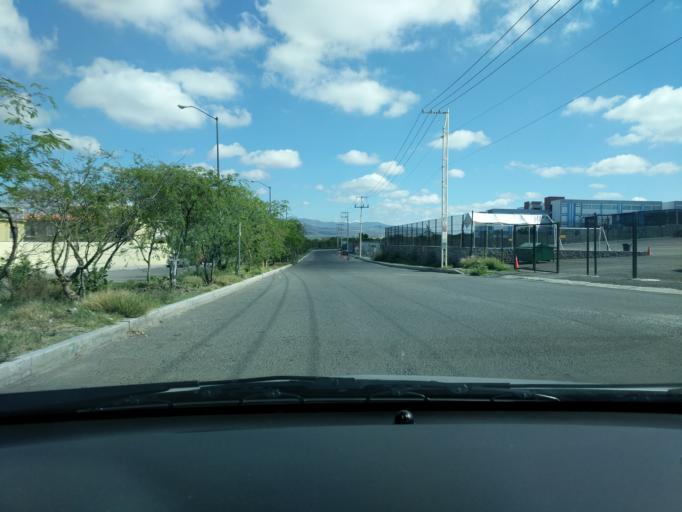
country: MX
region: Queretaro
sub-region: Queretaro
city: Patria Nueva
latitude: 20.6461
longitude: -100.4830
